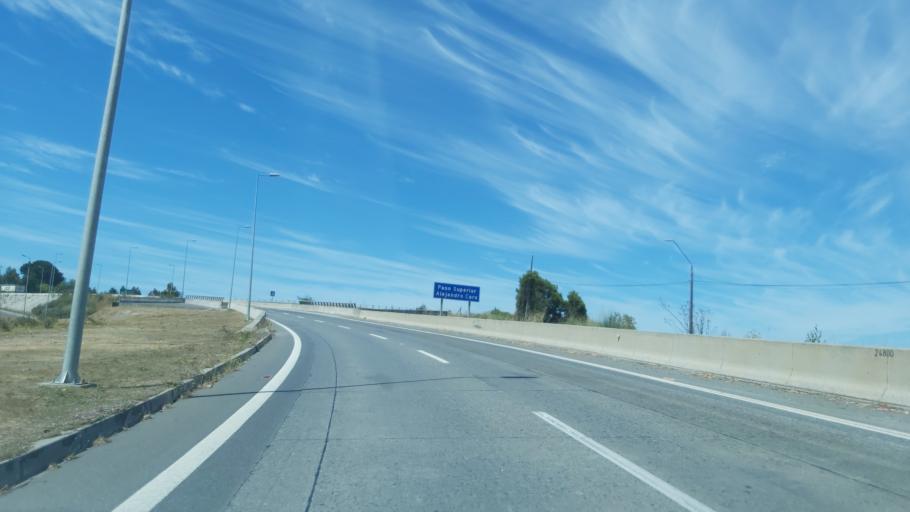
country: CL
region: Biobio
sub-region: Provincia de Concepcion
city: Coronel
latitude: -37.0465
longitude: -73.1423
